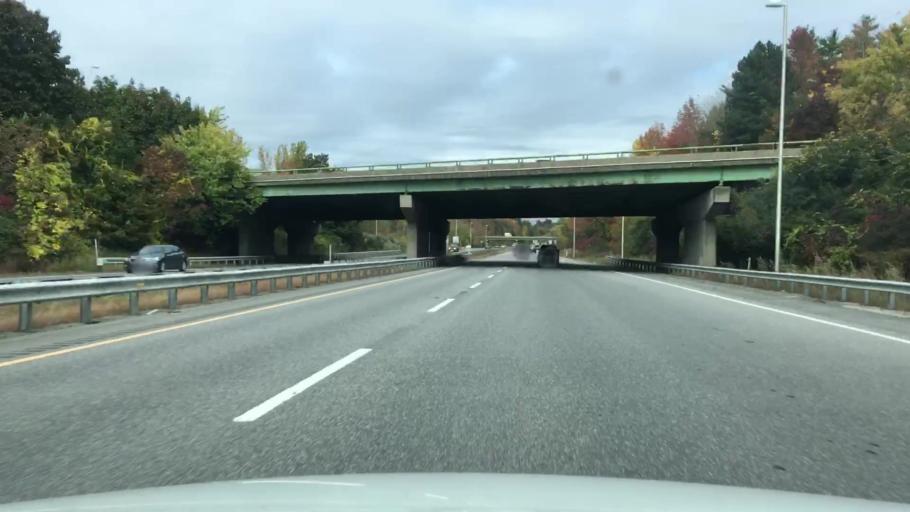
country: US
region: Maine
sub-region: Kennebec County
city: Augusta
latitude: 44.3159
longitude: -69.8112
